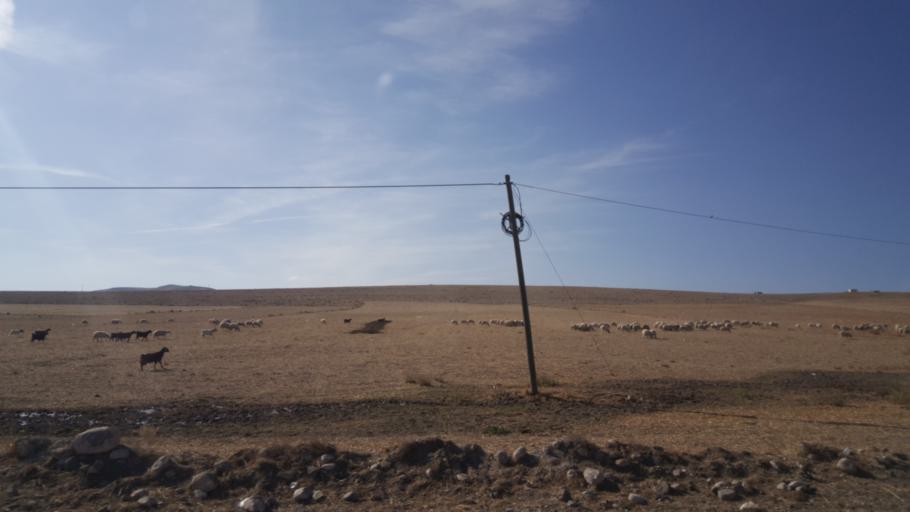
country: TR
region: Ankara
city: Altpinar
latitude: 39.2331
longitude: 32.7425
